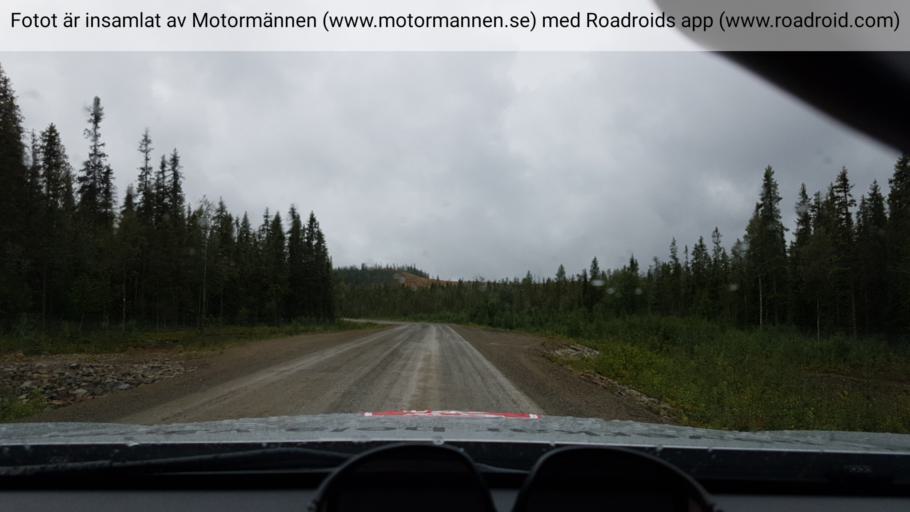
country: SE
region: Vaesterbotten
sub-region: Lycksele Kommun
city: Soderfors
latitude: 64.7832
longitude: 17.6514
